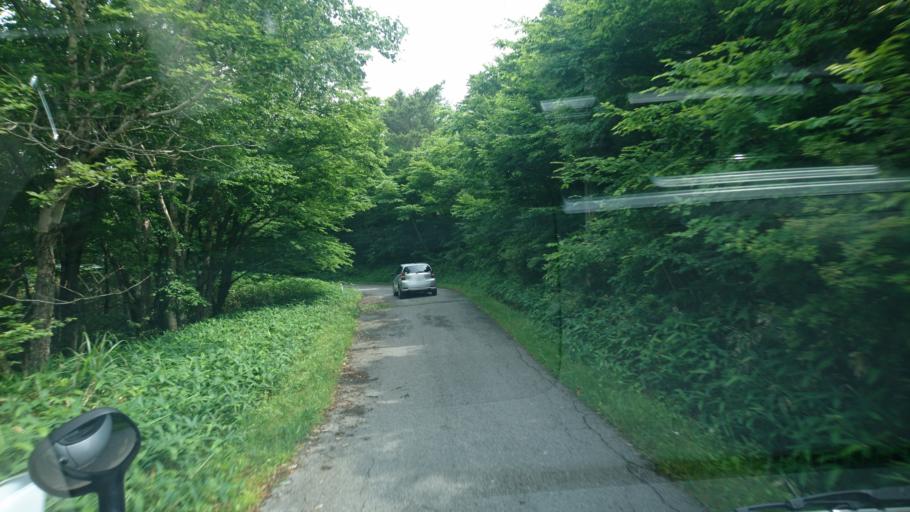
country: JP
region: Iwate
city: Ofunato
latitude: 39.1479
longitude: 141.7537
